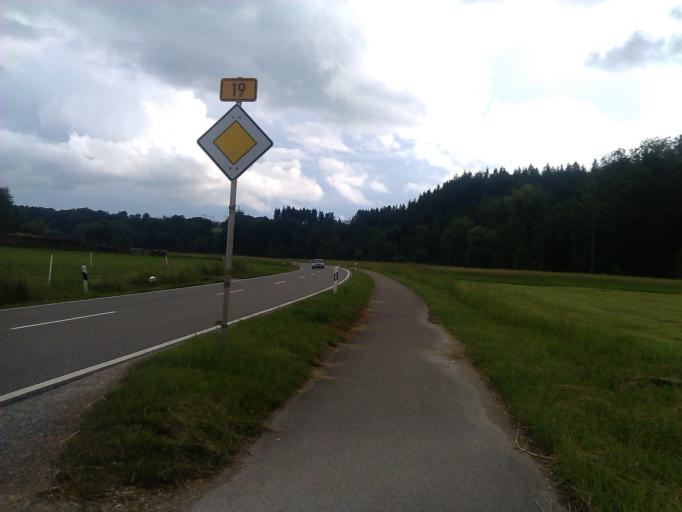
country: DE
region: Baden-Wuerttemberg
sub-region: Regierungsbezirk Stuttgart
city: Abtsgmund
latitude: 48.9003
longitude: 9.9919
